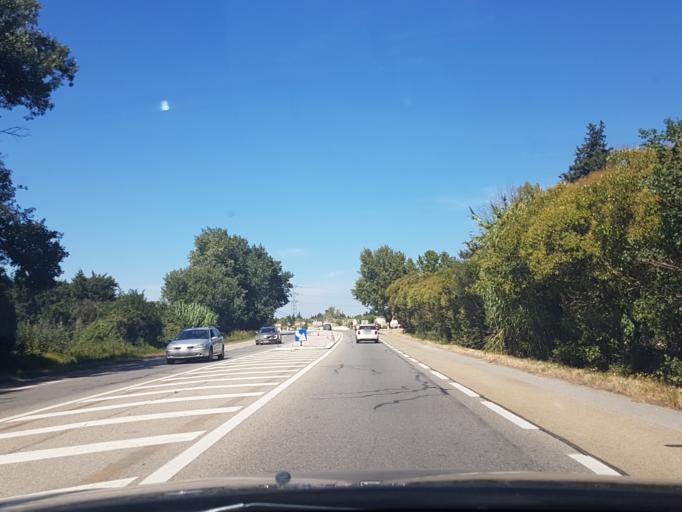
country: FR
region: Provence-Alpes-Cote d'Azur
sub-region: Departement des Bouches-du-Rhone
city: Rognonas
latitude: 43.9052
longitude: 4.8151
